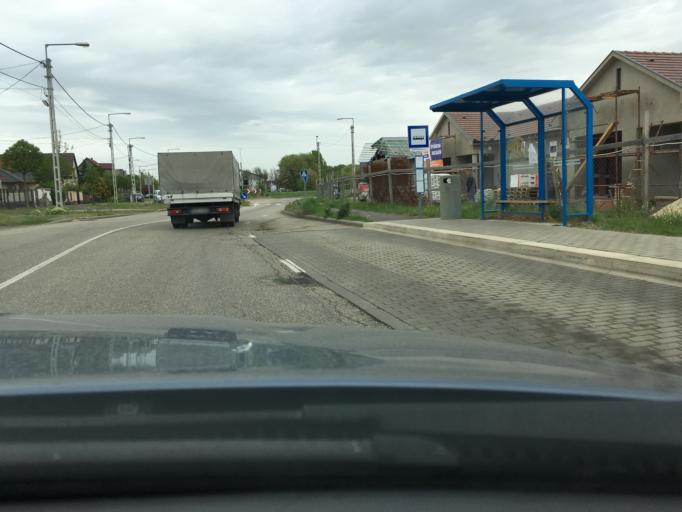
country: HU
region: Hajdu-Bihar
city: Debrecen
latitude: 47.5391
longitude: 21.6714
